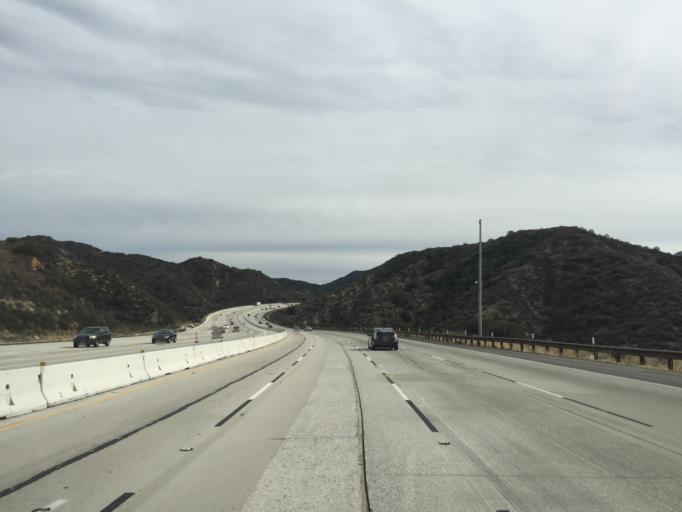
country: US
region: California
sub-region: Los Angeles County
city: Burbank
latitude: 34.2429
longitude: -118.3170
